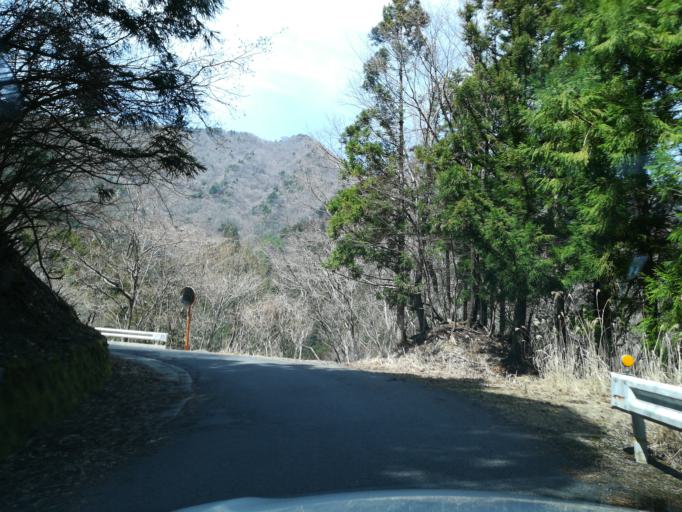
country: JP
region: Tokushima
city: Wakimachi
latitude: 33.8875
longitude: 134.0530
